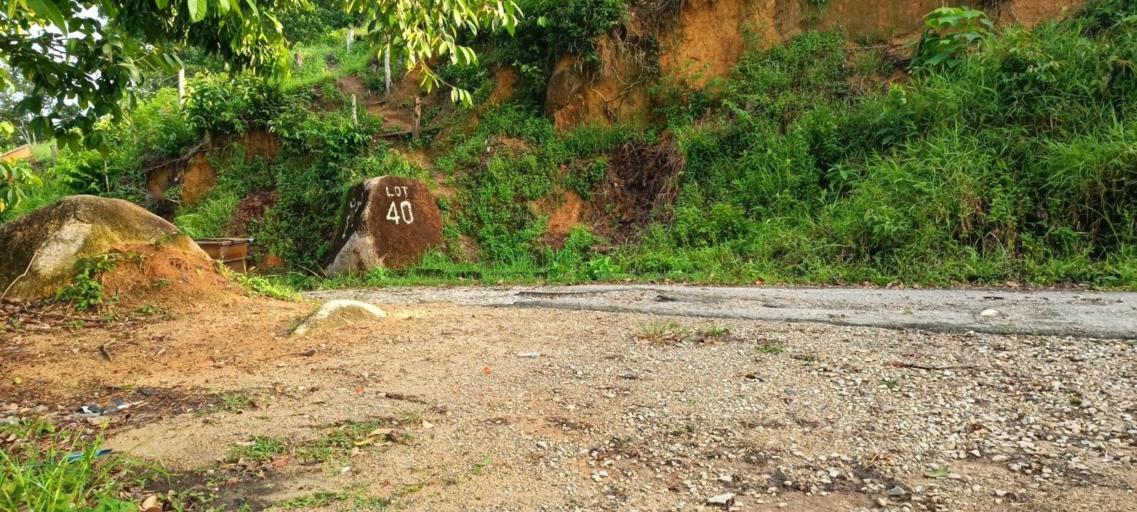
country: MY
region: Penang
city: Bukit Mertajam
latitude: 5.4051
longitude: 100.5058
